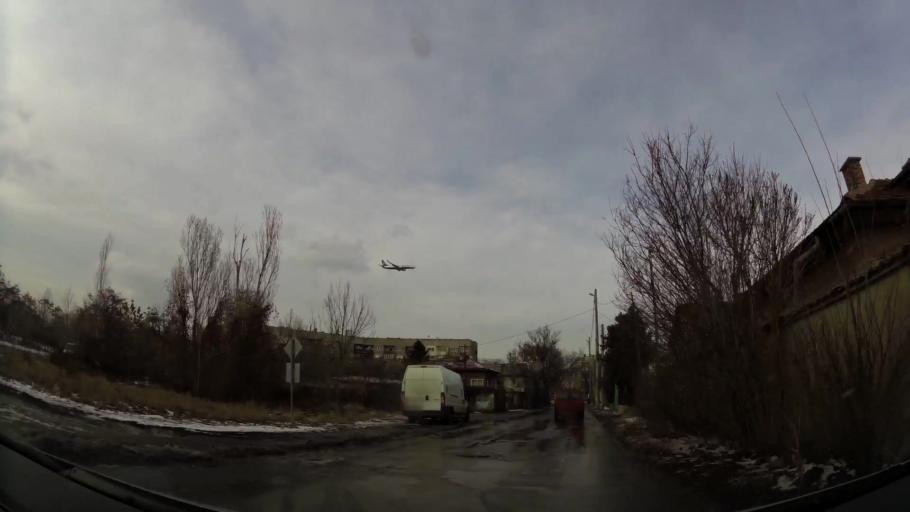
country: BG
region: Sofia-Capital
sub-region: Stolichna Obshtina
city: Sofia
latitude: 42.6952
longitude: 23.3750
